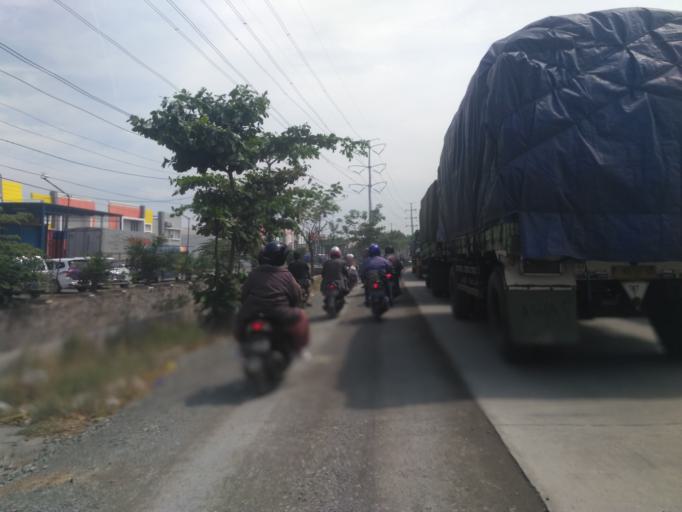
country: ID
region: Central Java
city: Semarang
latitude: -6.9553
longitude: 110.4140
